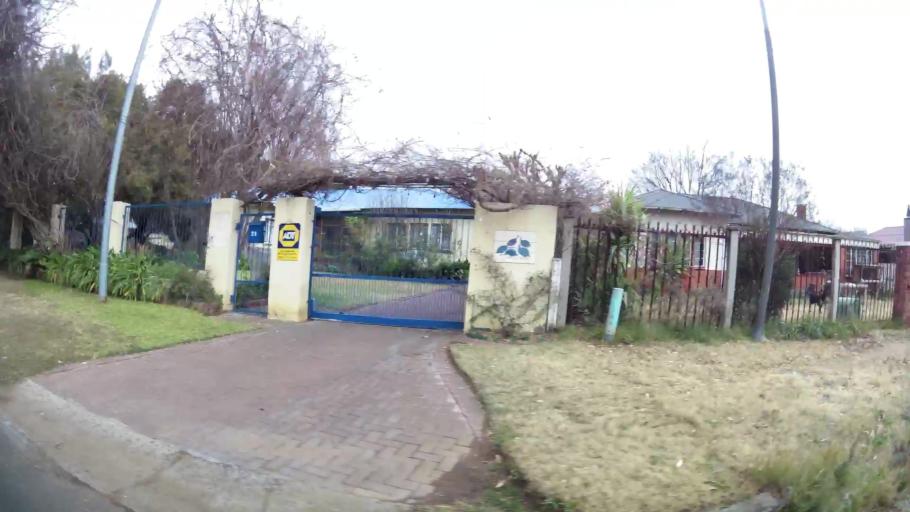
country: ZA
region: Orange Free State
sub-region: Mangaung Metropolitan Municipality
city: Bloemfontein
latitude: -29.1202
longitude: 26.1970
